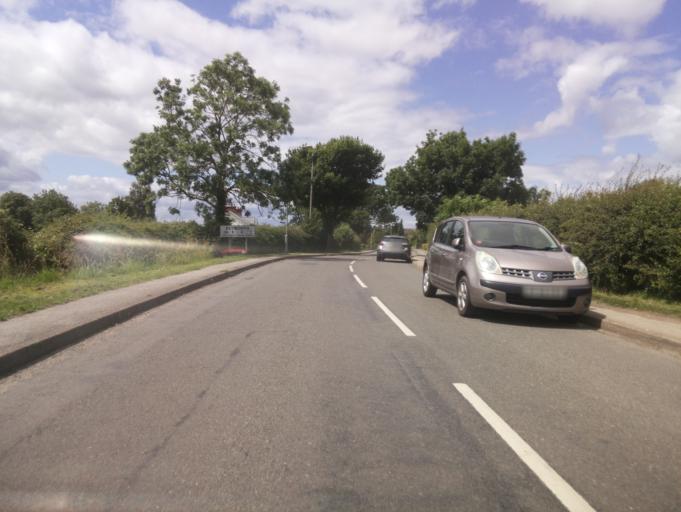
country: GB
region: England
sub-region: Nottinghamshire
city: Cotgrave
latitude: 52.8692
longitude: -1.0751
